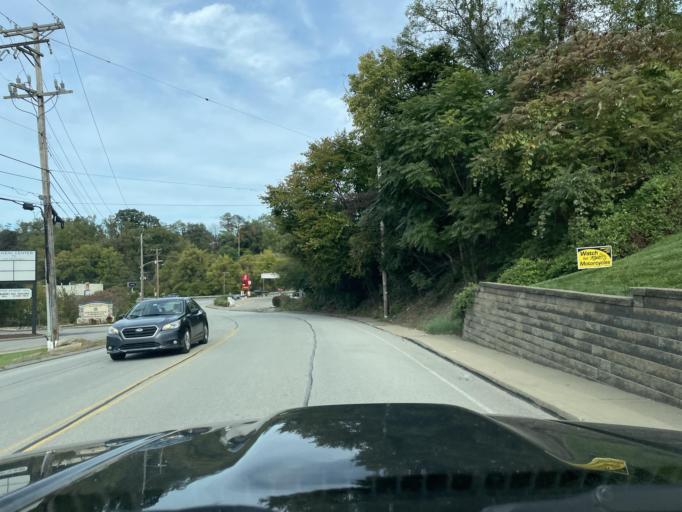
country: US
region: Pennsylvania
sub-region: Allegheny County
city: Monroeville
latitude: 40.4430
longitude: -79.7673
